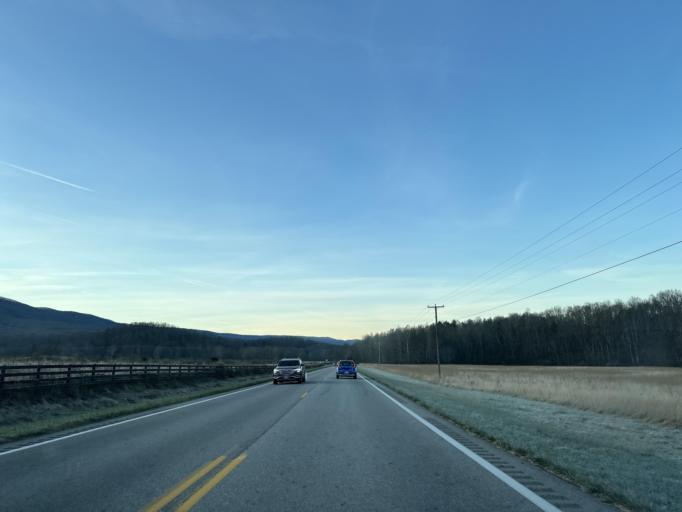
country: US
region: Virginia
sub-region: Augusta County
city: Jolivue
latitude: 38.1183
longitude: -79.2890
